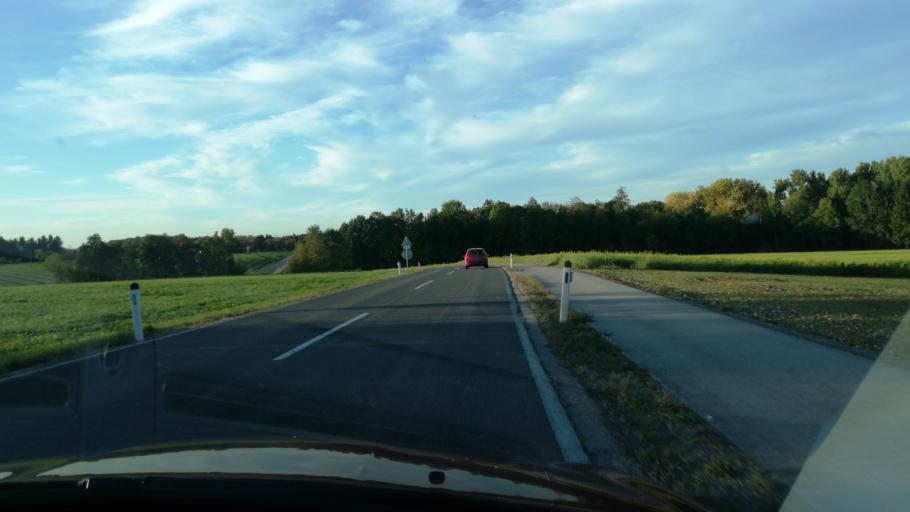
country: AT
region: Upper Austria
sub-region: Politischer Bezirk Steyr-Land
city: Waldneukirchen
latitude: 48.0101
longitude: 14.2466
